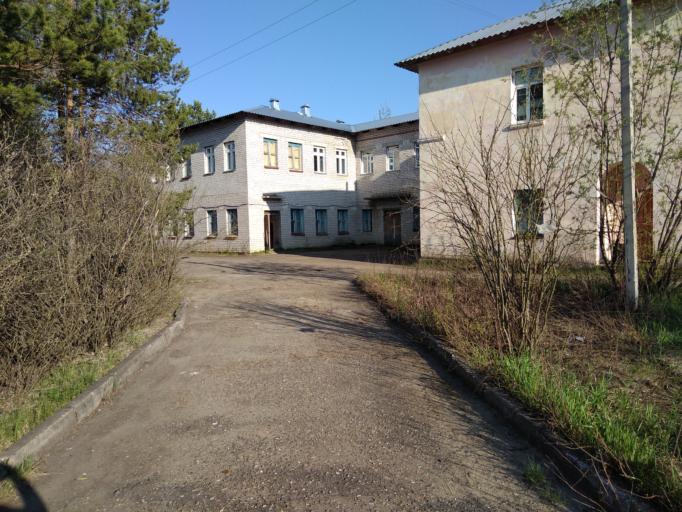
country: RU
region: Komi Republic
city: Puteyets
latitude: 65.1090
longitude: 57.1447
